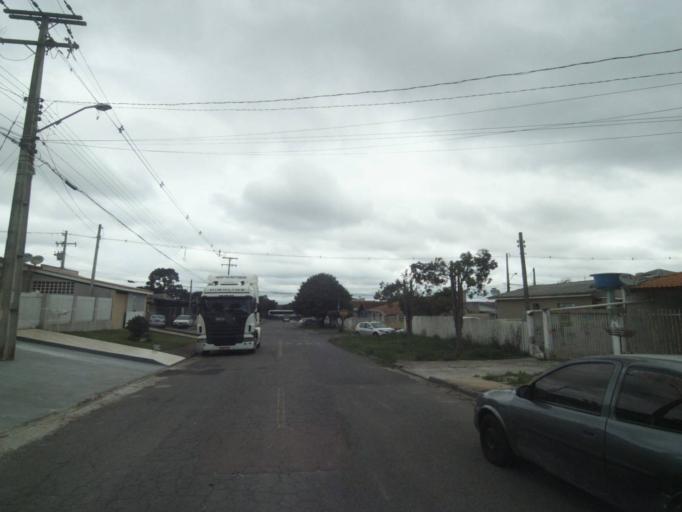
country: BR
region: Parana
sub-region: Sao Jose Dos Pinhais
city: Sao Jose dos Pinhais
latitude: -25.5501
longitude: -49.2745
